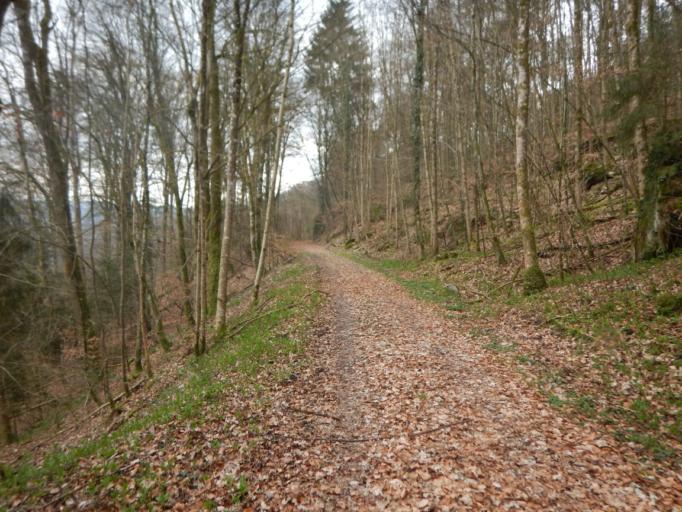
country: LU
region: Grevenmacher
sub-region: Canton d'Echternach
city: Beaufort
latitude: 49.8391
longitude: 6.3182
